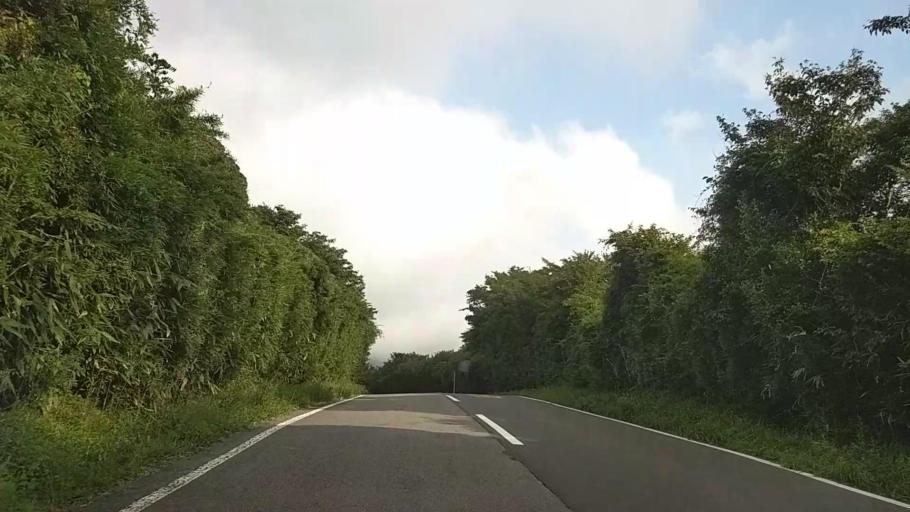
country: JP
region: Kanagawa
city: Hakone
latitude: 35.1837
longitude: 139.0076
